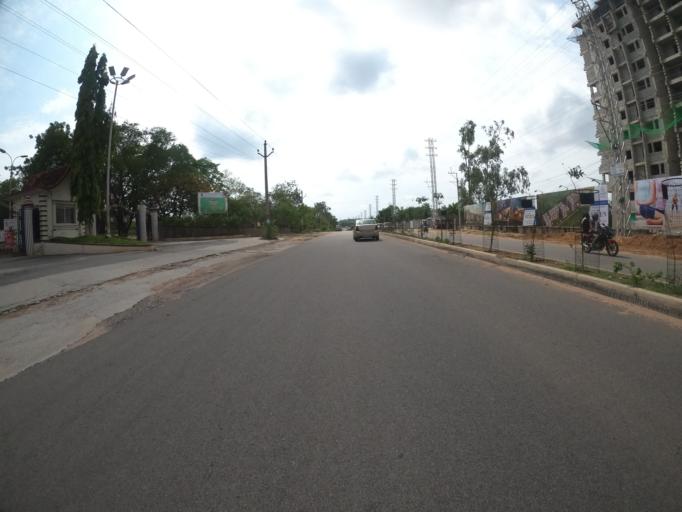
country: IN
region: Telangana
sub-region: Medak
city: Serilingampalle
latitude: 17.3921
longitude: 78.3227
